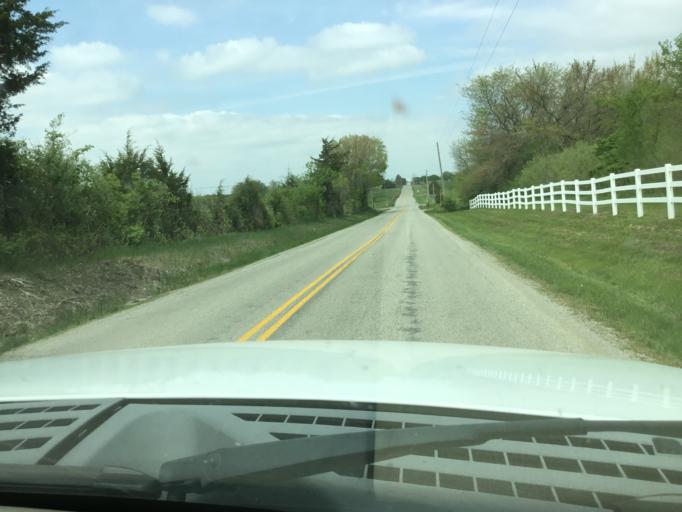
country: US
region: Kansas
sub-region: Shawnee County
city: Topeka
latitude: 38.9700
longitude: -95.6142
